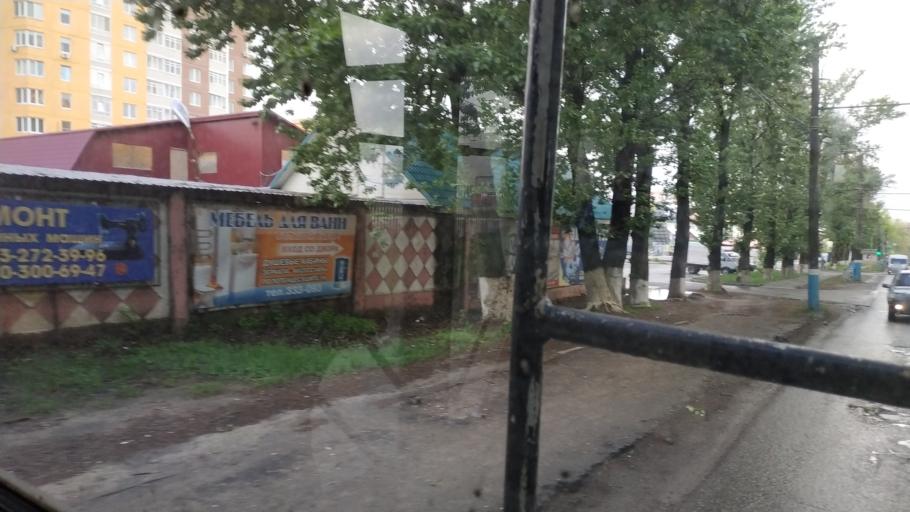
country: RU
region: Brjansk
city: Putevka
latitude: 53.2626
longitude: 34.3243
